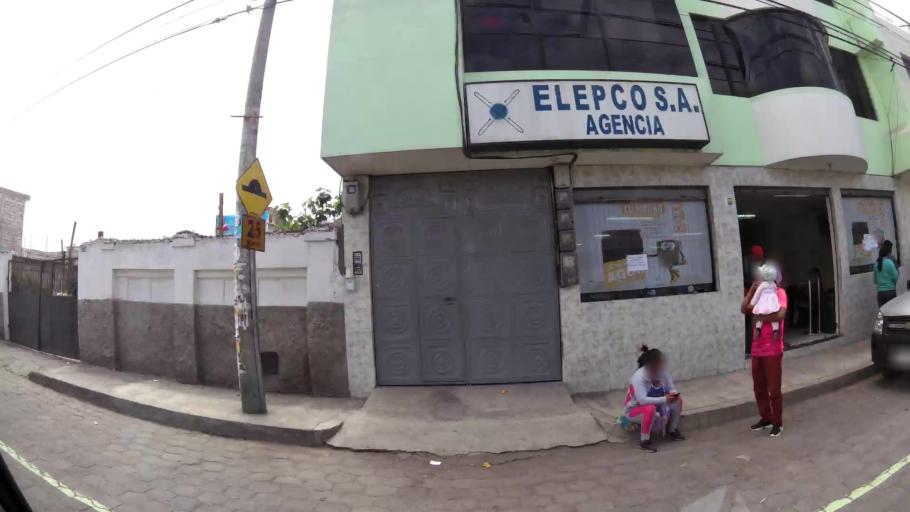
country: EC
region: Cotopaxi
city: San Miguel de Salcedo
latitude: -1.0454
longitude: -78.5884
